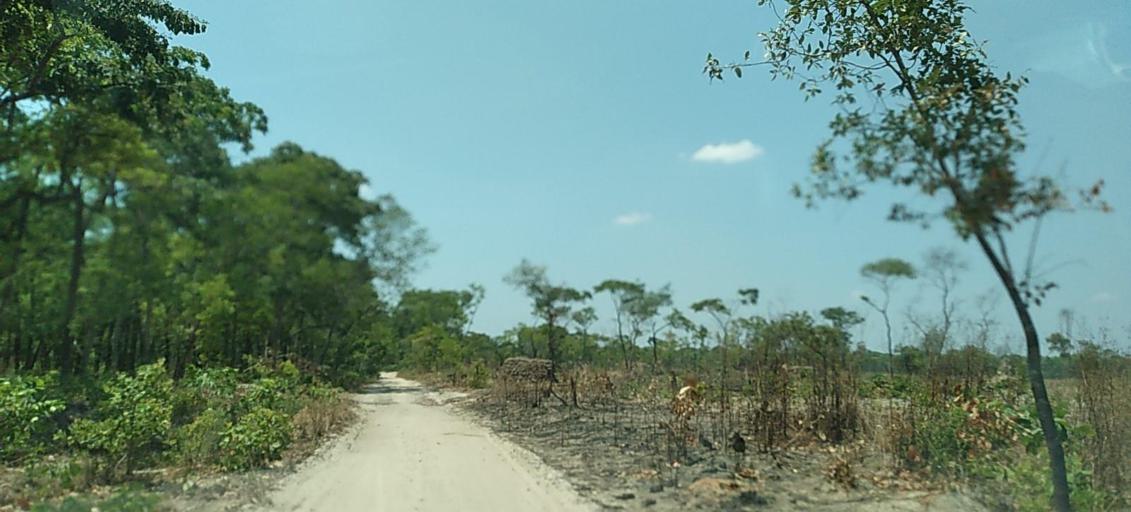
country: ZM
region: Copperbelt
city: Mpongwe
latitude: -13.6356
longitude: 28.4811
